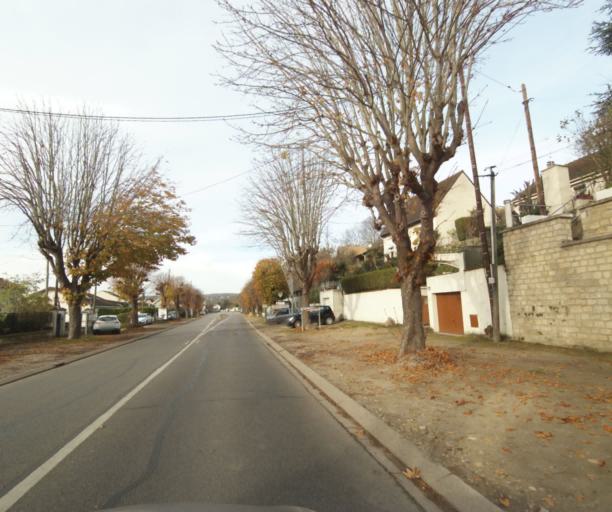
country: FR
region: Ile-de-France
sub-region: Departement des Yvelines
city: Vernouillet
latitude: 48.9944
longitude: 1.9863
